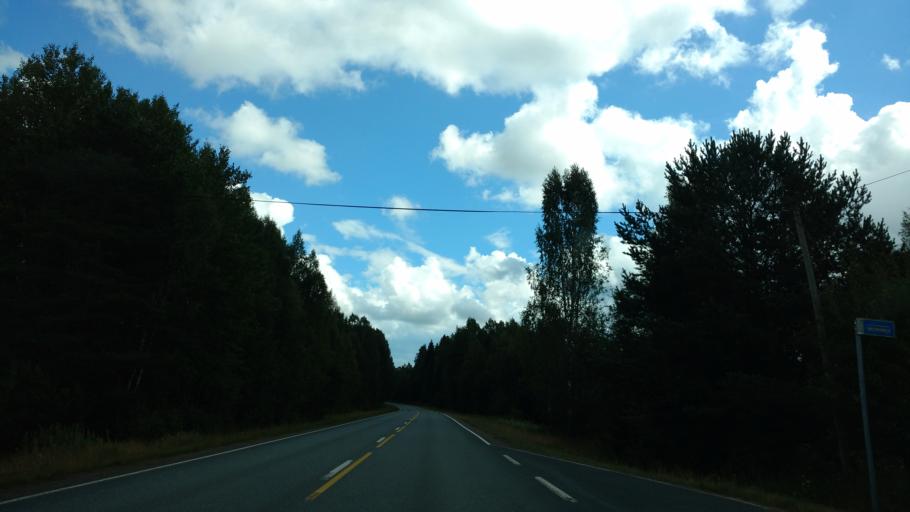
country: FI
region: Varsinais-Suomi
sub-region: Salo
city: Kisko
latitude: 60.2419
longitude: 23.5473
